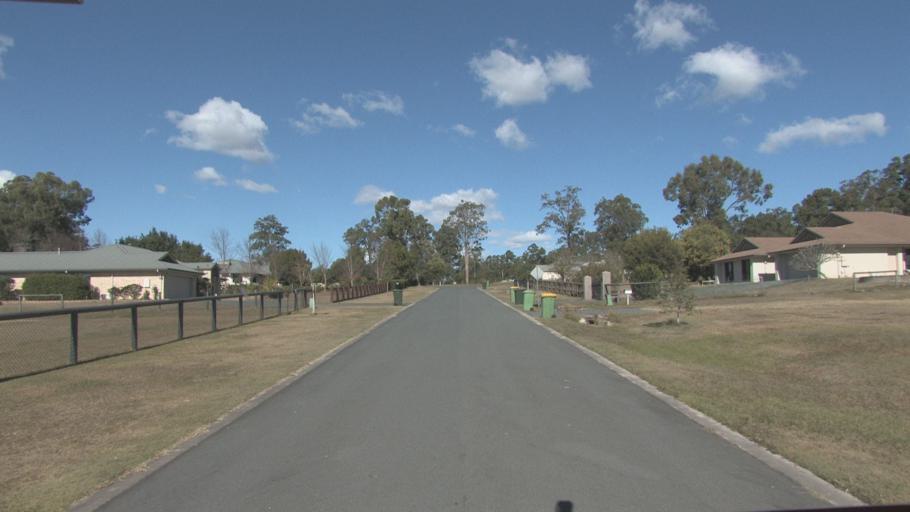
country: AU
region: Queensland
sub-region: Logan
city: North Maclean
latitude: -27.7535
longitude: 152.9591
